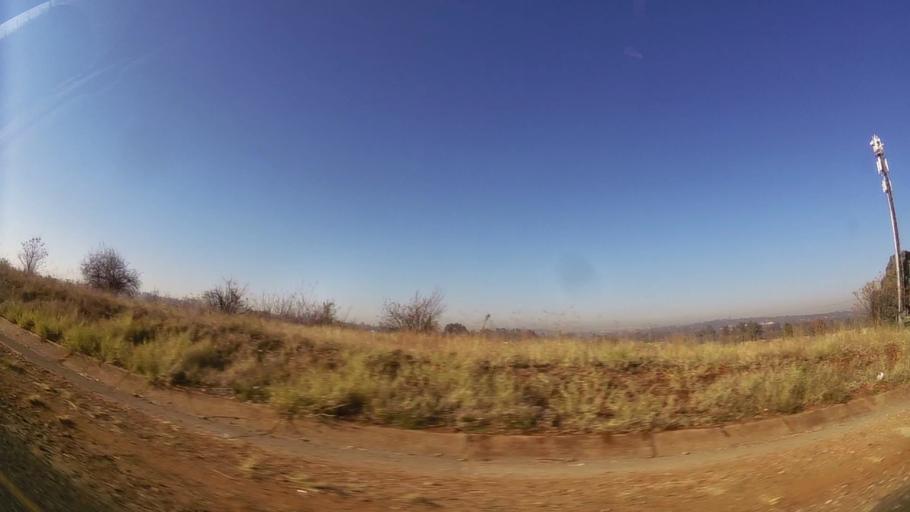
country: ZA
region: Gauteng
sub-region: City of Tshwane Metropolitan Municipality
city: Centurion
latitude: -25.8229
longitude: 28.1667
